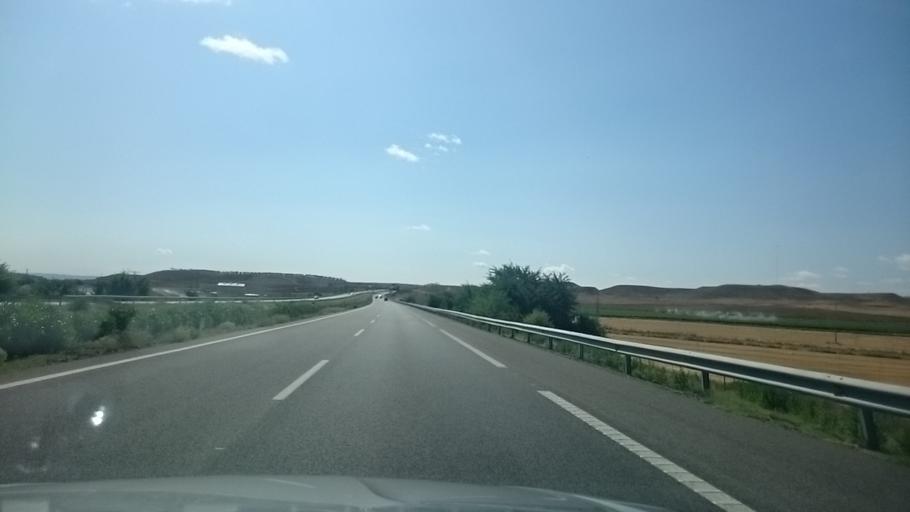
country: ES
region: Navarre
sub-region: Provincia de Navarra
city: Fontellas
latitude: 41.9832
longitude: -1.5641
